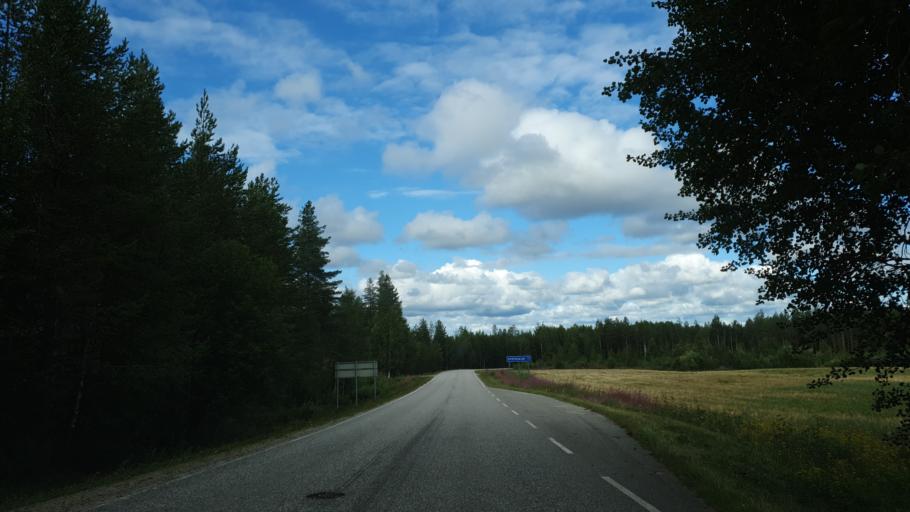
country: FI
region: Kainuu
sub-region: Kehys-Kainuu
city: Kuhmo
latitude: 64.1970
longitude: 29.1694
